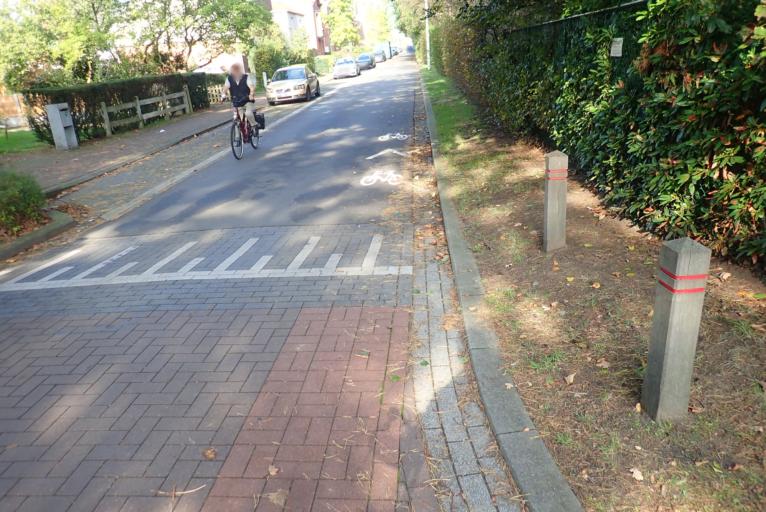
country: BE
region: Flanders
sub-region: Provincie Antwerpen
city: Kapellen
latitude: 51.3099
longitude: 4.4338
